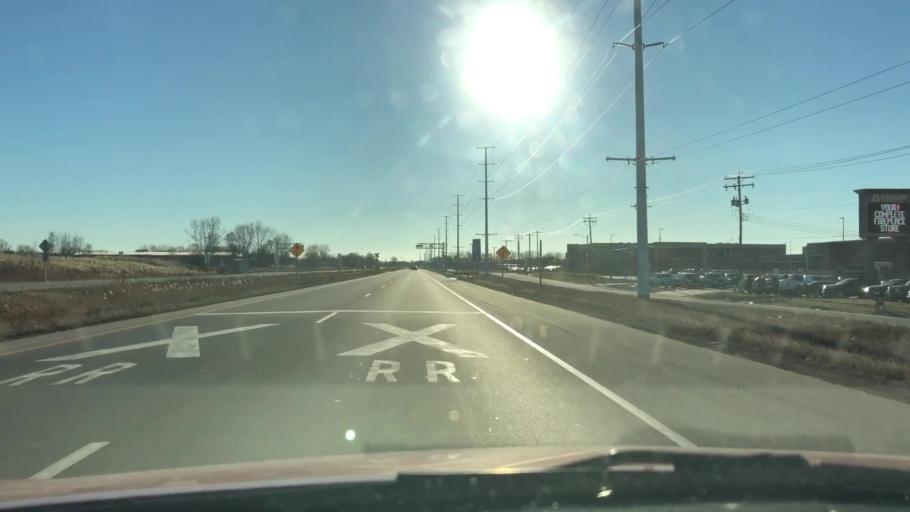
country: US
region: Wisconsin
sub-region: Brown County
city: Ashwaubenon
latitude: 44.4717
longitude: -88.0649
